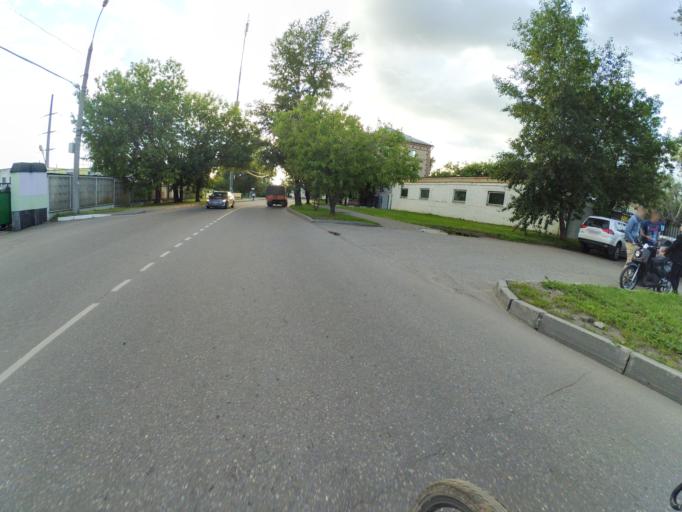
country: RU
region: Moscow
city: Strogino
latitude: 55.8377
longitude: 37.4373
